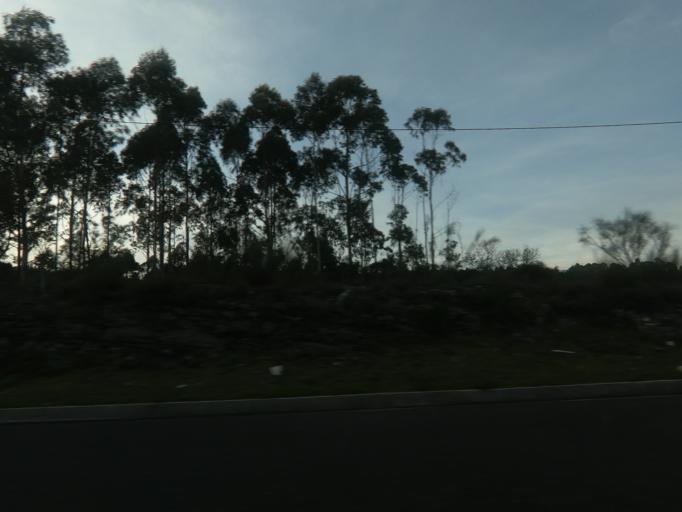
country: PT
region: Leiria
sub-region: Leiria
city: Santa Catarina da Serra
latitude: 39.6639
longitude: -8.6907
